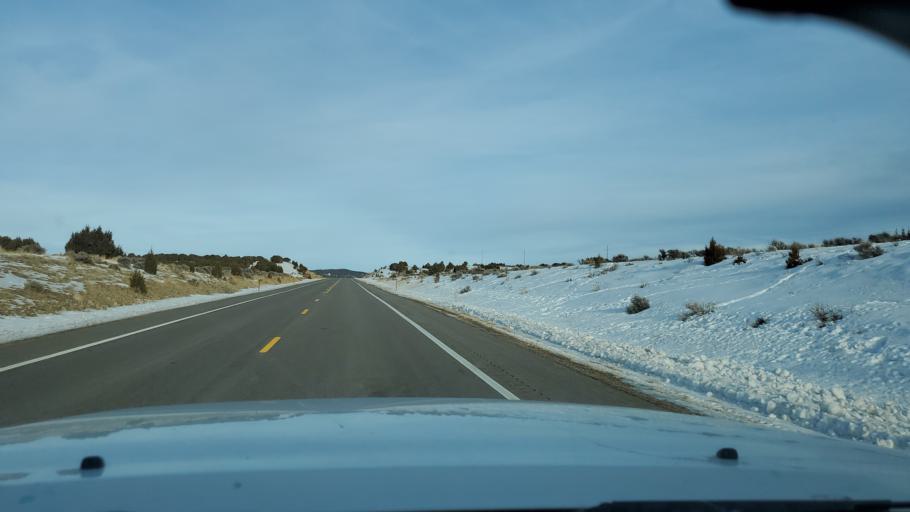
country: US
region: Colorado
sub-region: Rio Blanco County
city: Rangely
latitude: 40.3352
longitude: -108.4800
